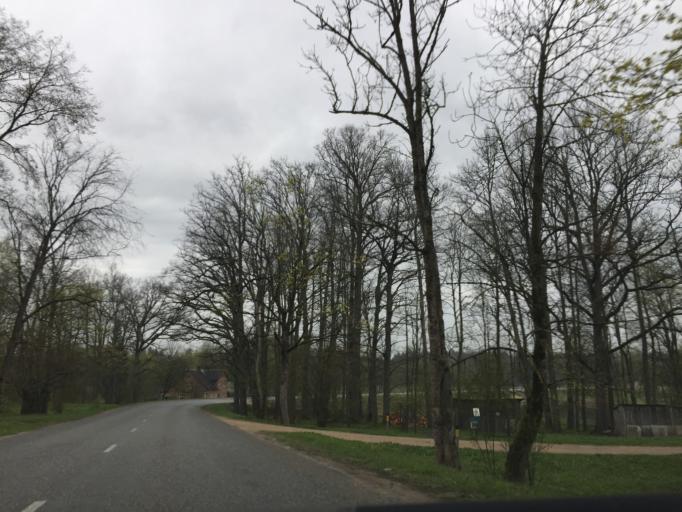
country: LV
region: Sigulda
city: Sigulda
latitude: 57.0277
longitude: 24.8166
